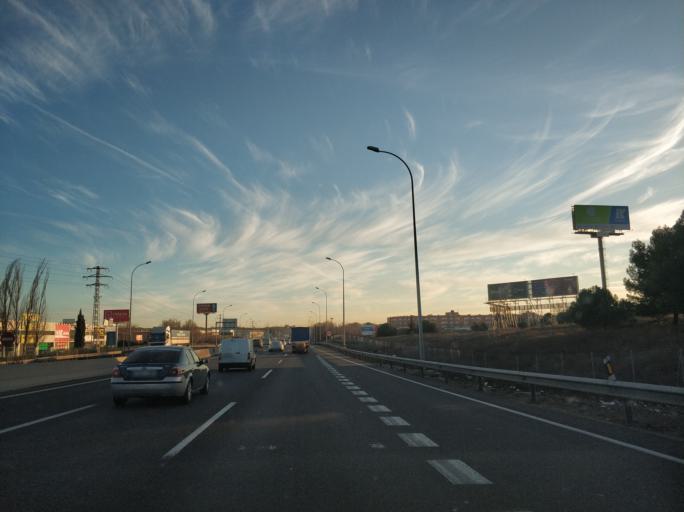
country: ES
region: Madrid
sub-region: Provincia de Madrid
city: Pinto
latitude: 40.2634
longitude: -3.6906
